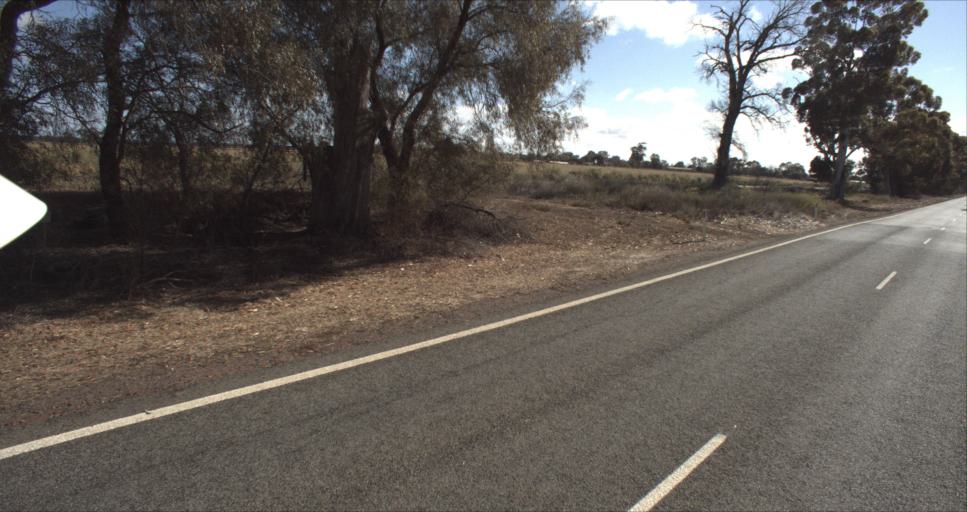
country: AU
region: New South Wales
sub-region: Leeton
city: Leeton
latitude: -34.5478
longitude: 146.3229
